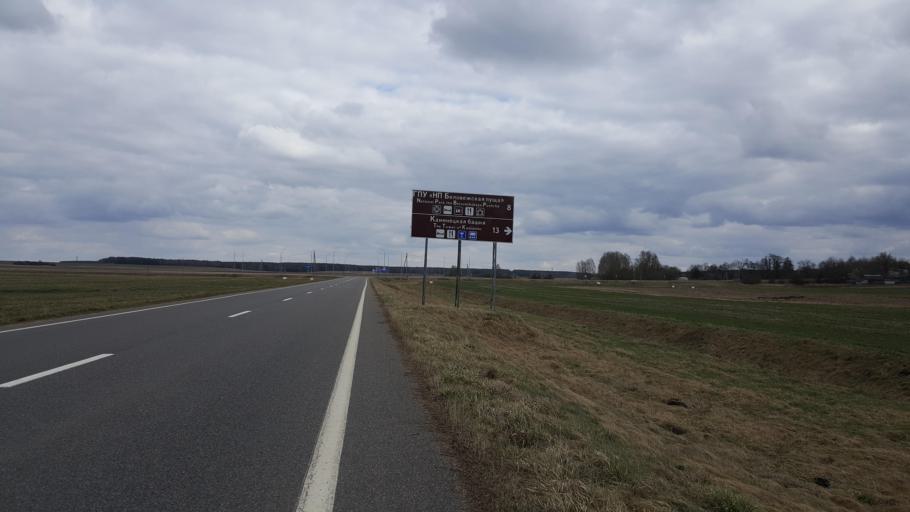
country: BY
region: Brest
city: Kamyanyuki
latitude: 52.4962
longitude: 23.7784
